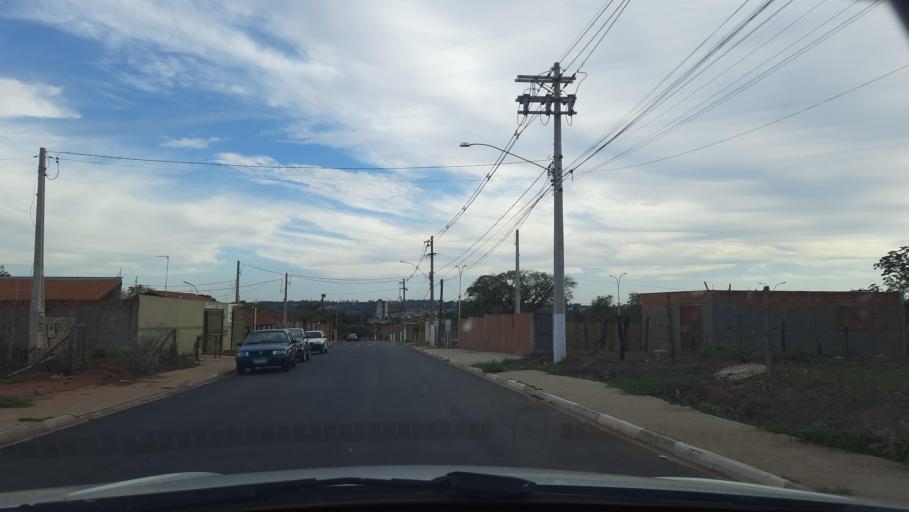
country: BR
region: Sao Paulo
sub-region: Casa Branca
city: Casa Branca
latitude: -21.7613
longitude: -47.0853
